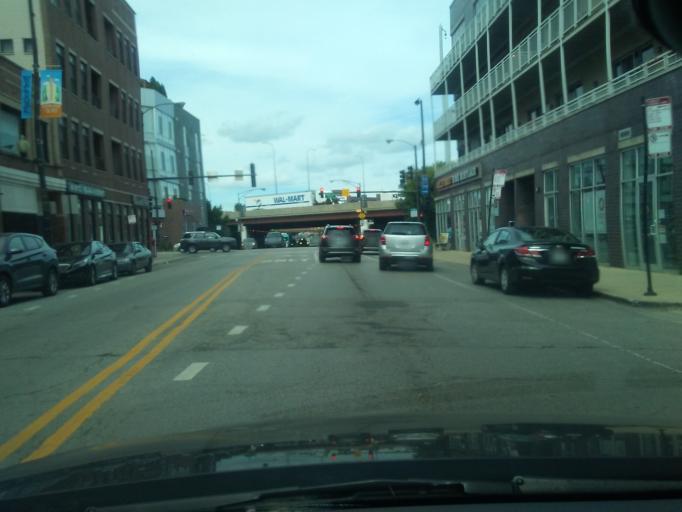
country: US
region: Illinois
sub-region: Cook County
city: Chicago
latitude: 41.9209
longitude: -87.6777
